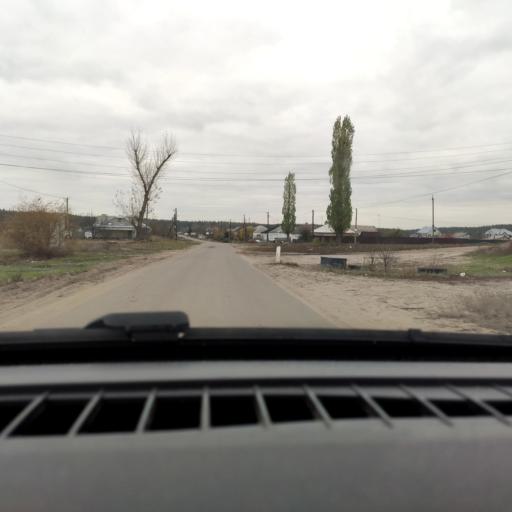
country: RU
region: Voronezj
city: Maslovka
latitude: 51.5799
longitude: 39.3024
